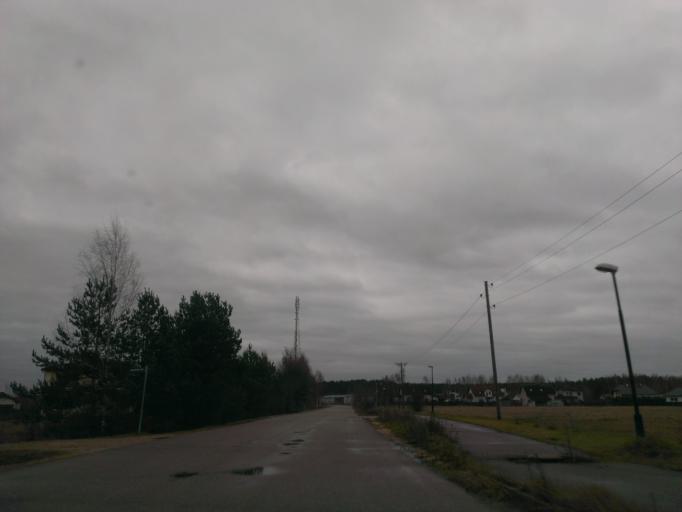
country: LV
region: Adazi
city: Adazi
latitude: 57.0687
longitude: 24.3322
